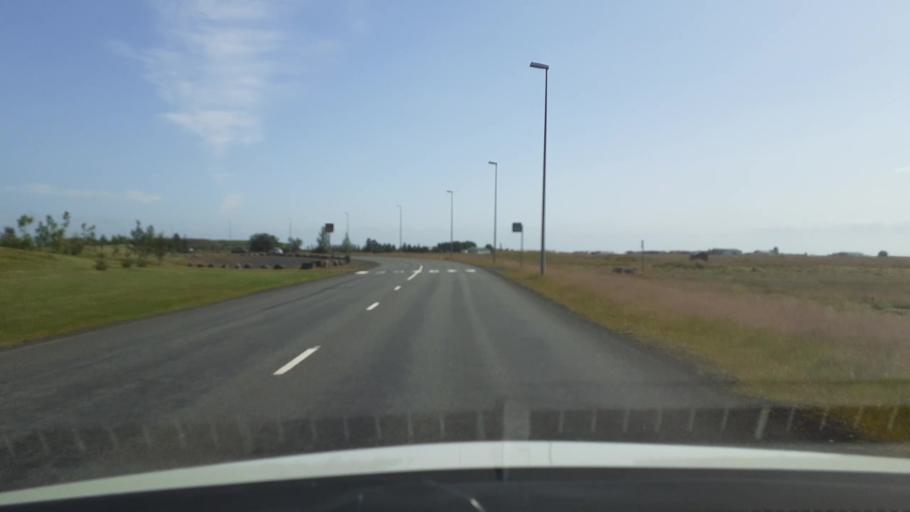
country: IS
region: South
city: Selfoss
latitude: 63.9230
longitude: -21.0078
